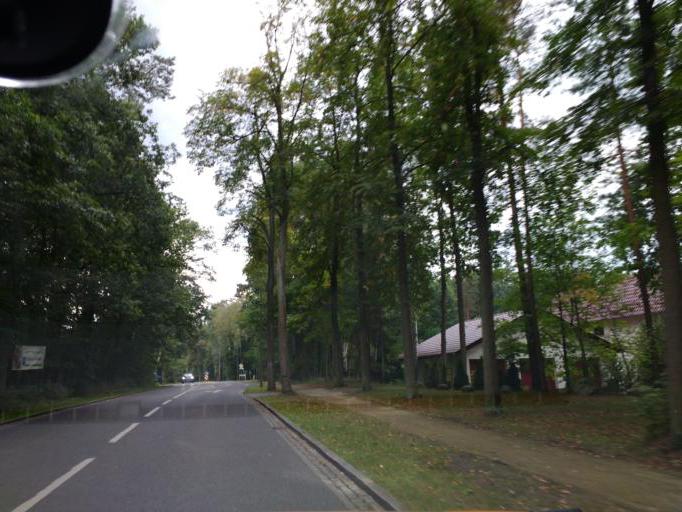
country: DE
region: Brandenburg
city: Bad Saarow
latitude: 52.2935
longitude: 14.0457
